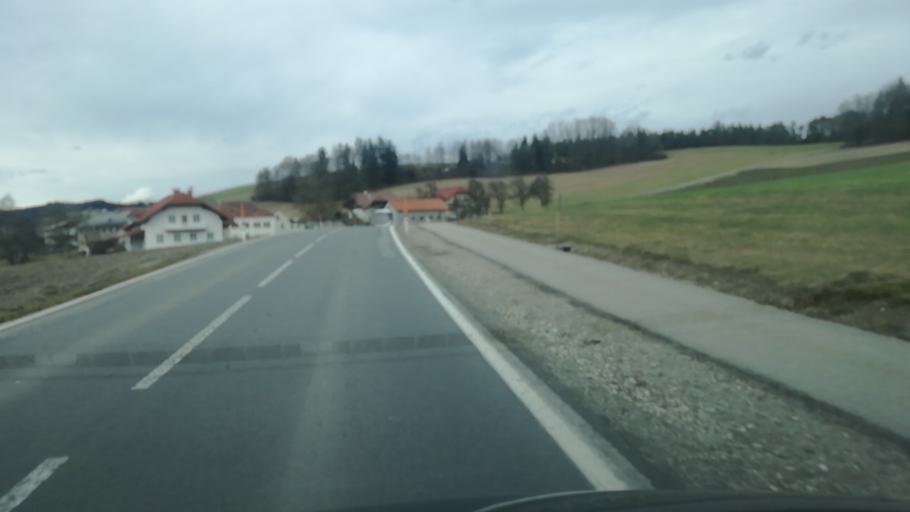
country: AT
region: Upper Austria
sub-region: Politischer Bezirk Vocklabruck
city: Frankenburg
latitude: 48.0781
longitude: 13.4890
